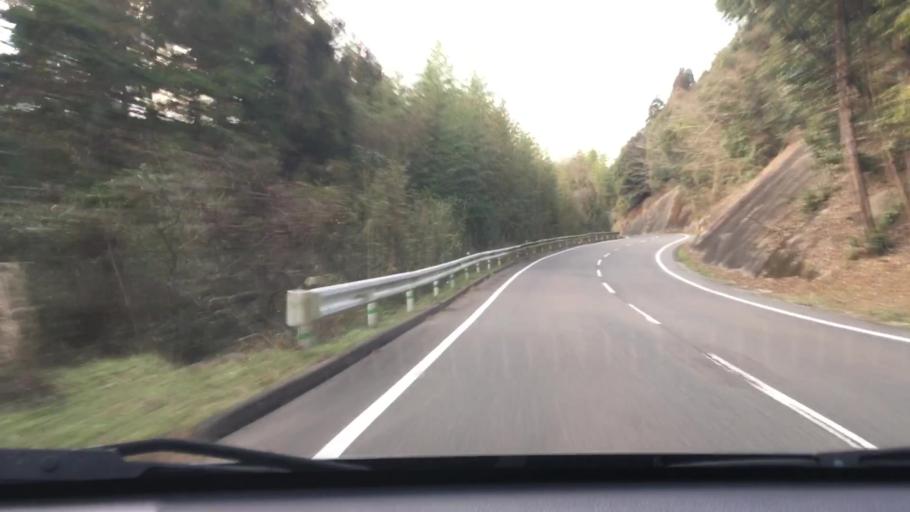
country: JP
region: Oita
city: Hiji
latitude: 33.4152
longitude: 131.4200
